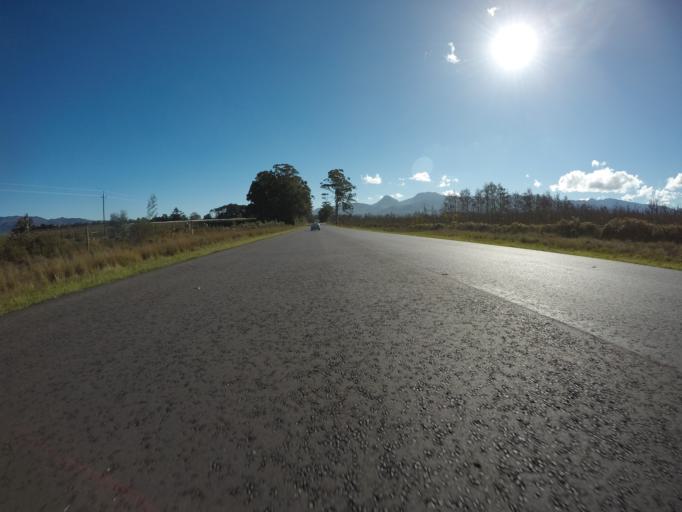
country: ZA
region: Western Cape
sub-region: Overberg District Municipality
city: Grabouw
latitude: -34.1710
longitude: 19.0476
